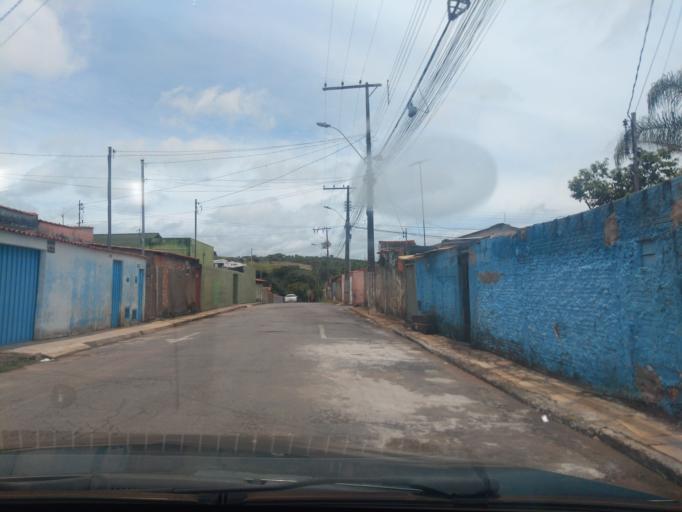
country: BR
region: Minas Gerais
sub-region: Tres Coracoes
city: Tres Coracoes
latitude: -21.6807
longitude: -45.2590
